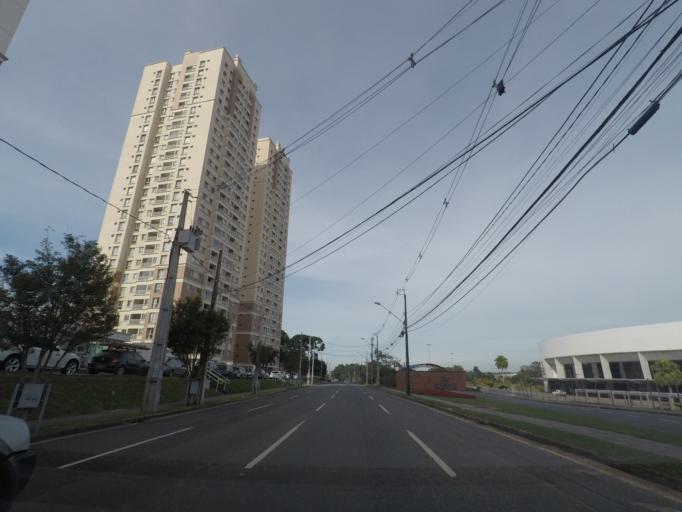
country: BR
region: Parana
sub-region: Curitiba
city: Curitiba
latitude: -25.4456
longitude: -49.3556
